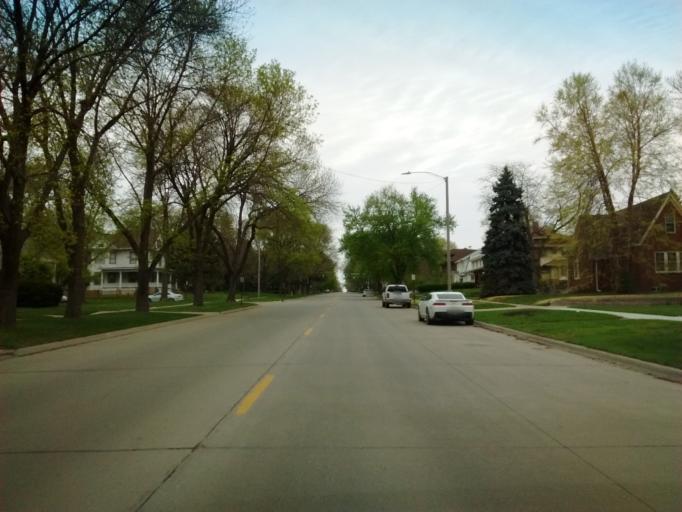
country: US
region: Iowa
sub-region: Woodbury County
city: Sioux City
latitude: 42.5165
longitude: -96.4022
